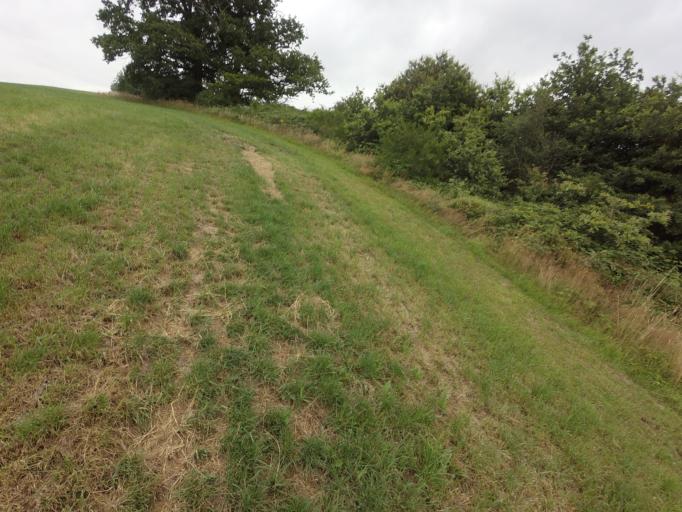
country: NL
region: Limburg
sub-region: Gemeente Vaals
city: Vaals
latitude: 50.7624
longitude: 6.0079
